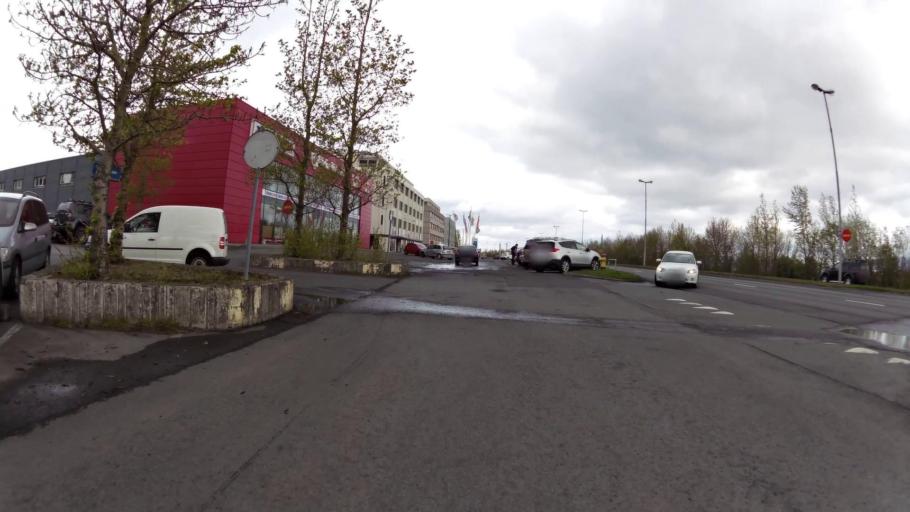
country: IS
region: Capital Region
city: Reykjavik
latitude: 64.1367
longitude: -21.8755
